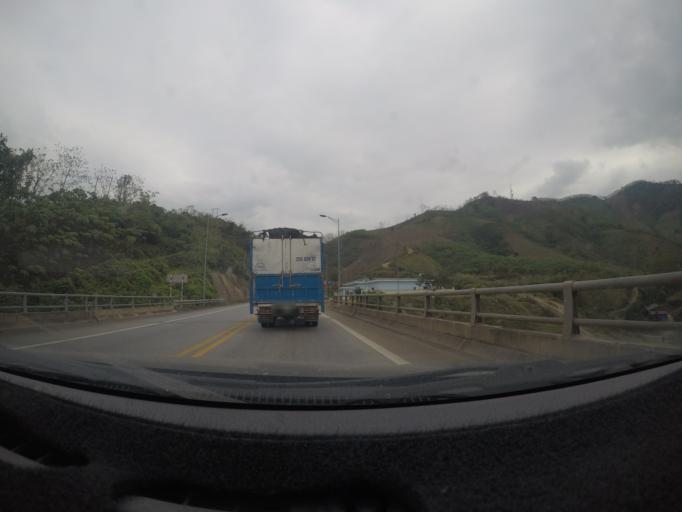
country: VN
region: Lao Cai
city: Thi Tran Pho Rang
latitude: 22.0963
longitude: 104.4265
